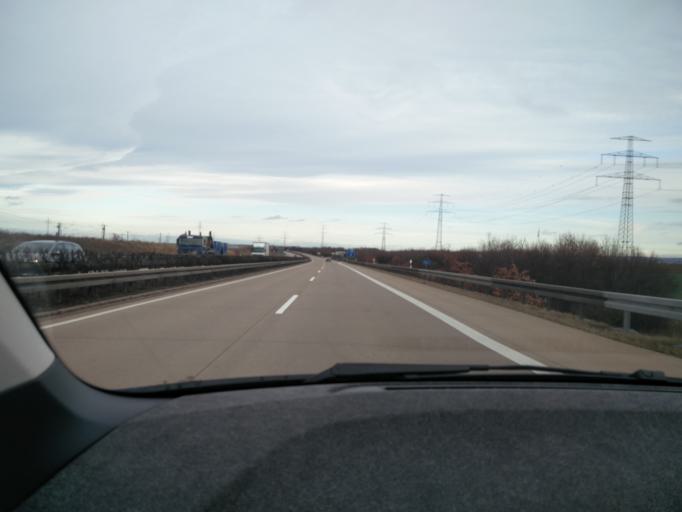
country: DE
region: Thuringia
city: Dornheim
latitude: 50.8315
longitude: 11.0086
